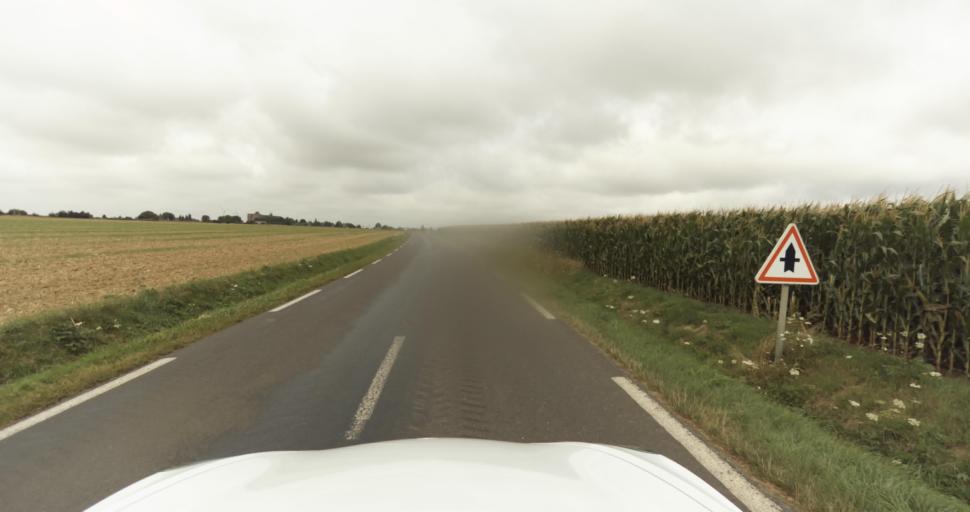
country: FR
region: Haute-Normandie
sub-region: Departement de l'Eure
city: Claville
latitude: 49.0851
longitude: 1.0504
